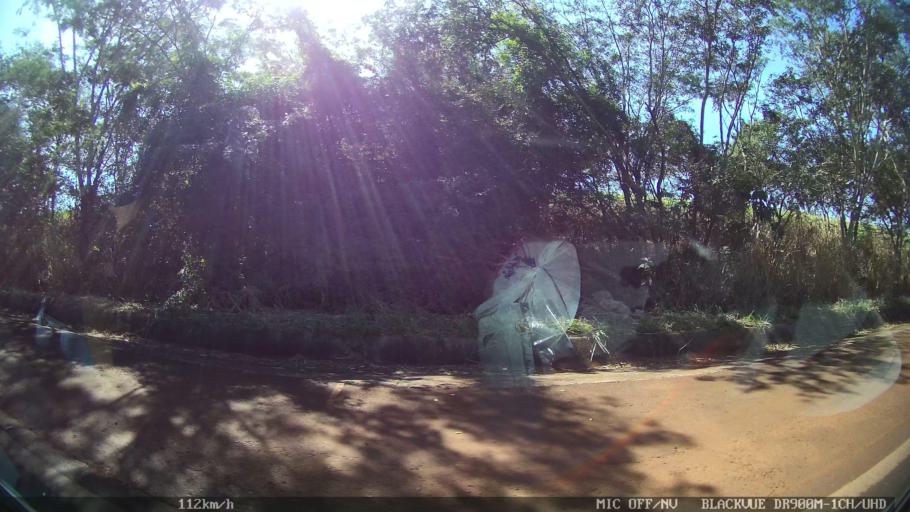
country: BR
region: Sao Paulo
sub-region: Sao Joaquim Da Barra
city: Sao Joaquim da Barra
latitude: -20.5379
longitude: -47.8232
